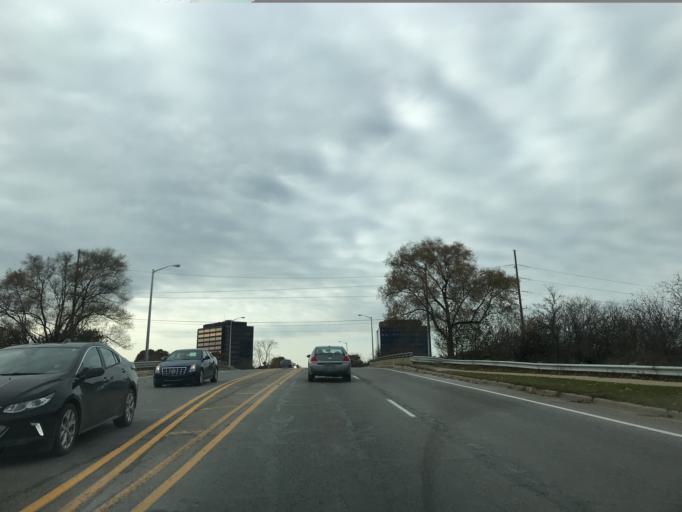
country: US
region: Michigan
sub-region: Washtenaw County
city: Ann Arbor
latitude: 42.2443
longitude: -83.7310
